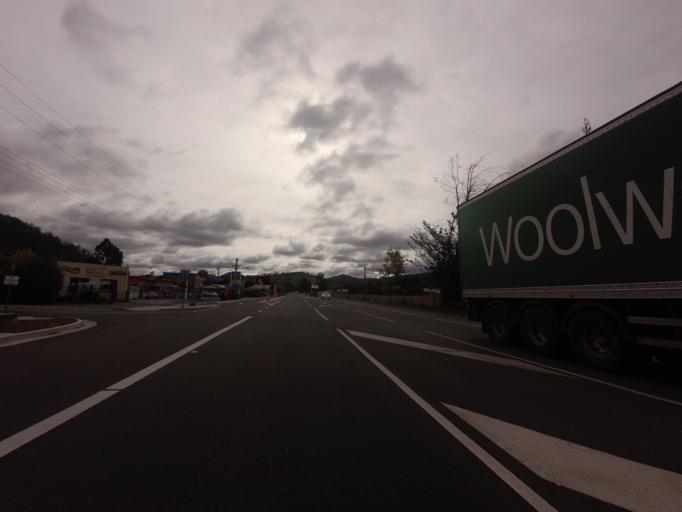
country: AU
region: Tasmania
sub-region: Brighton
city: Bridgewater
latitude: -42.6036
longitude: 147.2202
